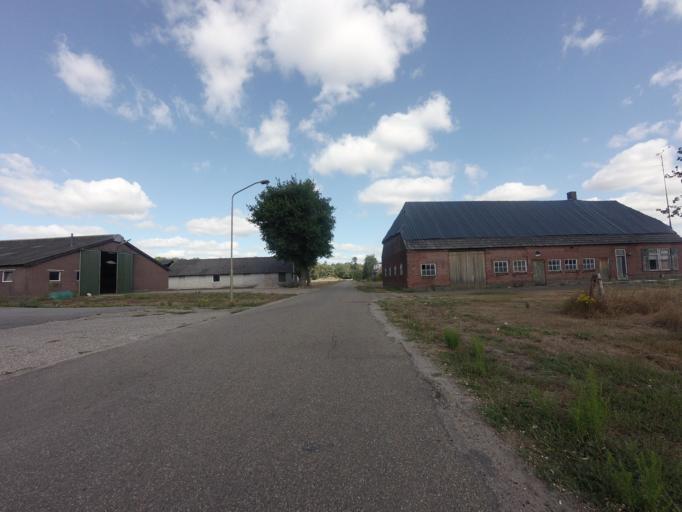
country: NL
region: North Brabant
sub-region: Gemeente Landerd
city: Schaijk
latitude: 51.7508
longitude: 5.6080
